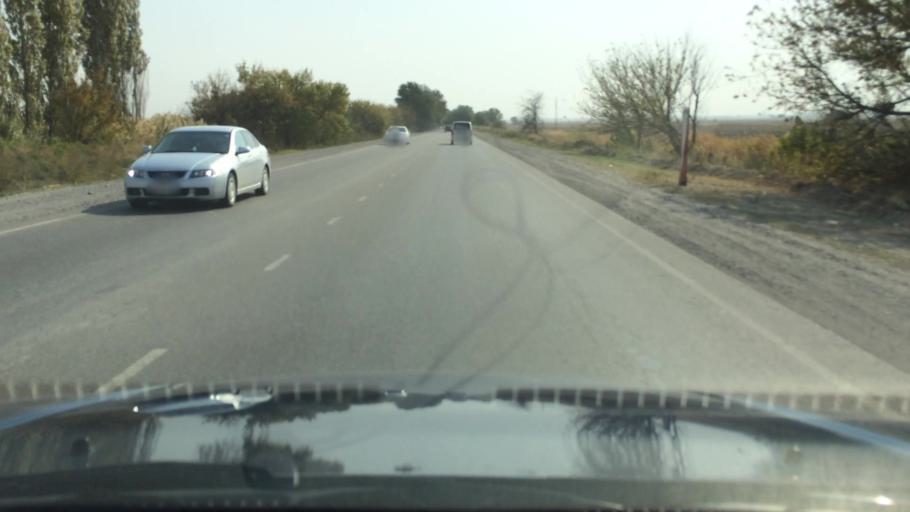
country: KG
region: Chuy
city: Lebedinovka
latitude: 42.9250
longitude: 74.7014
